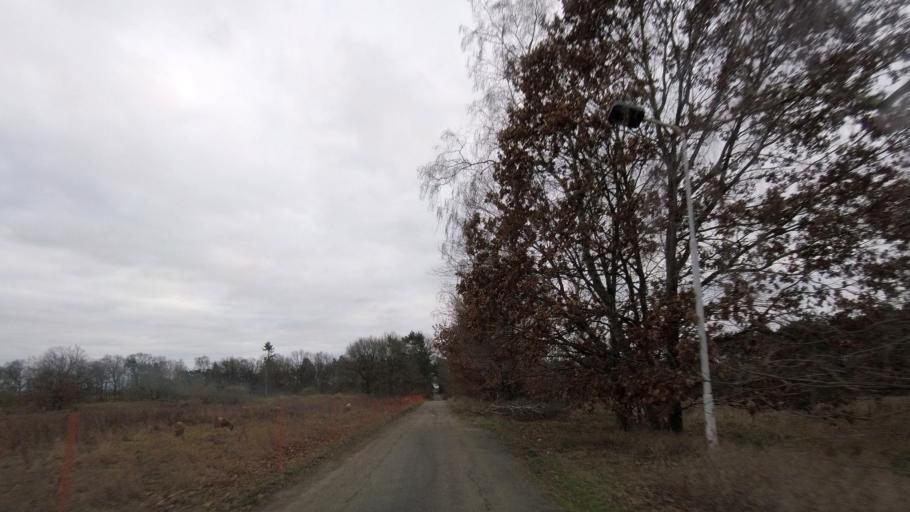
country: DE
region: Brandenburg
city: Niedergorsdorf
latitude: 51.9876
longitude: 12.9898
